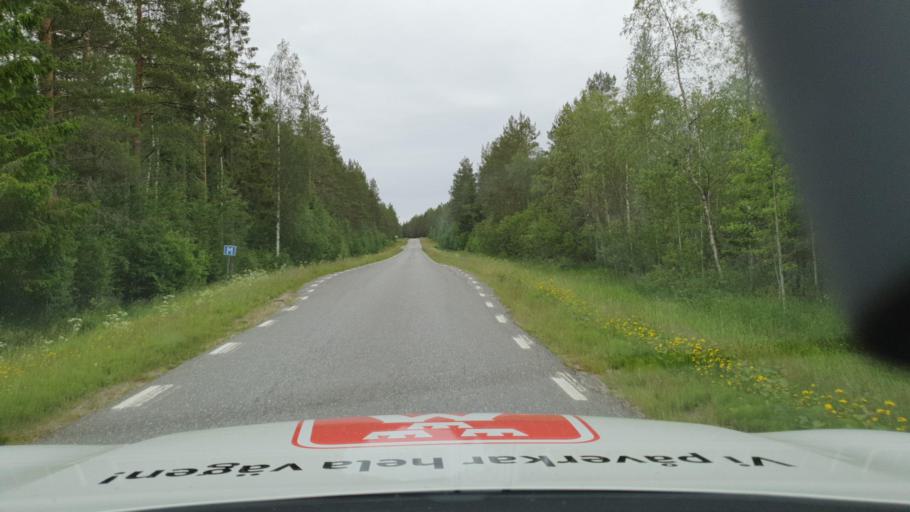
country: SE
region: Vaesterbotten
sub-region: Nordmalings Kommun
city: Nordmaling
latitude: 63.4914
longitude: 19.4373
